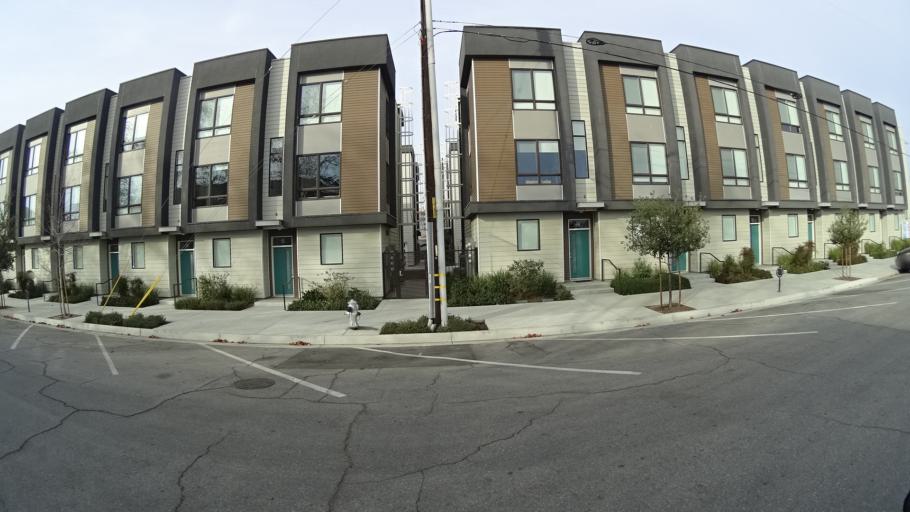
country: US
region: California
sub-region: Kern County
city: Bakersfield
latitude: 35.3750
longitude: -119.0129
